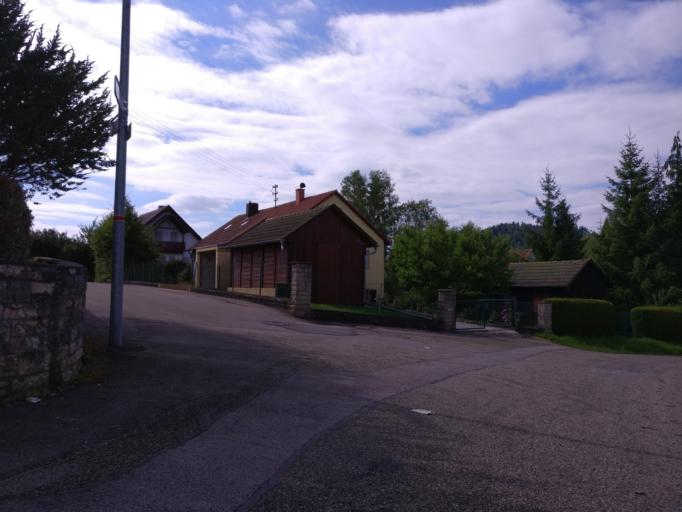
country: DE
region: Baden-Wuerttemberg
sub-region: Regierungsbezirk Stuttgart
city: Fichtenberg
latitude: 48.9818
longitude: 9.7097
